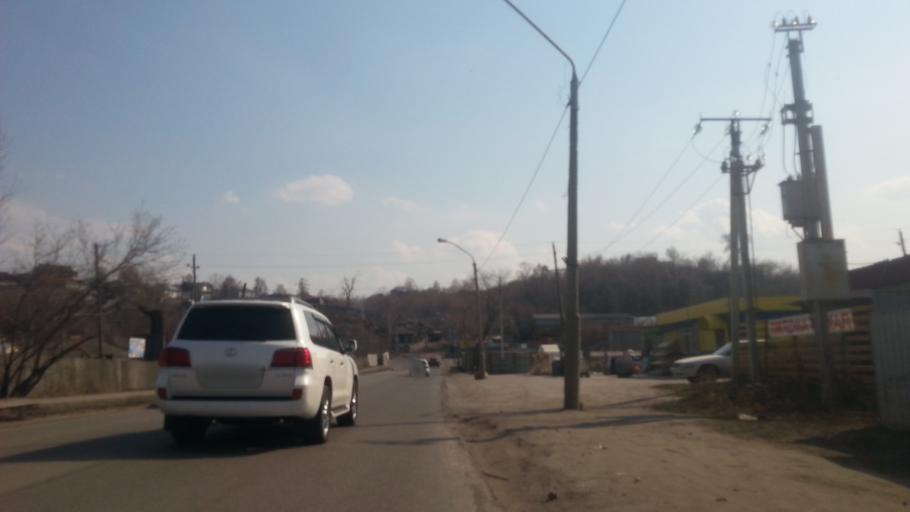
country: RU
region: Altai Krai
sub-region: Gorod Barnaulskiy
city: Barnaul
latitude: 53.3205
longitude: 83.7698
